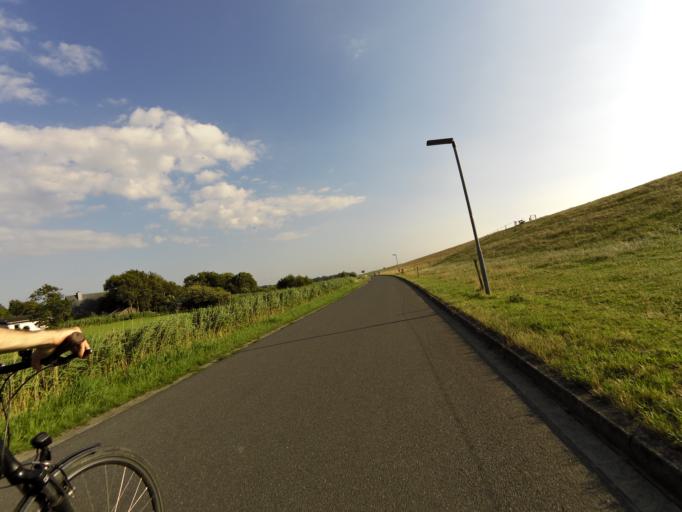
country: DE
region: Lower Saxony
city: Nordholz
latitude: 53.7847
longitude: 8.5514
